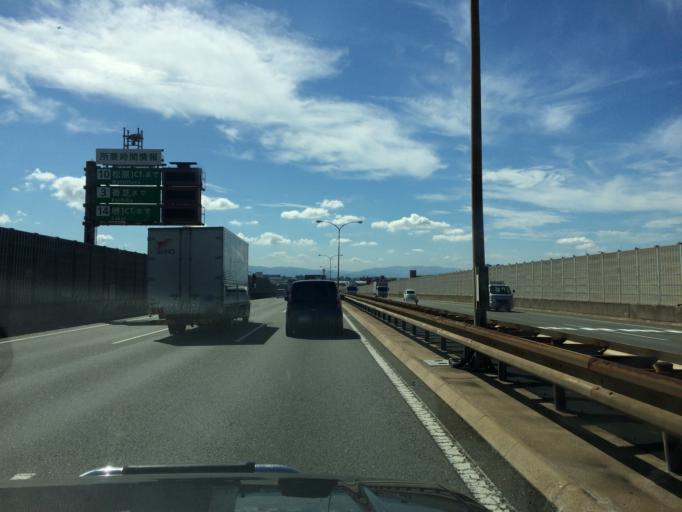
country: JP
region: Osaka
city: Yao
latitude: 34.6628
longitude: 135.5983
